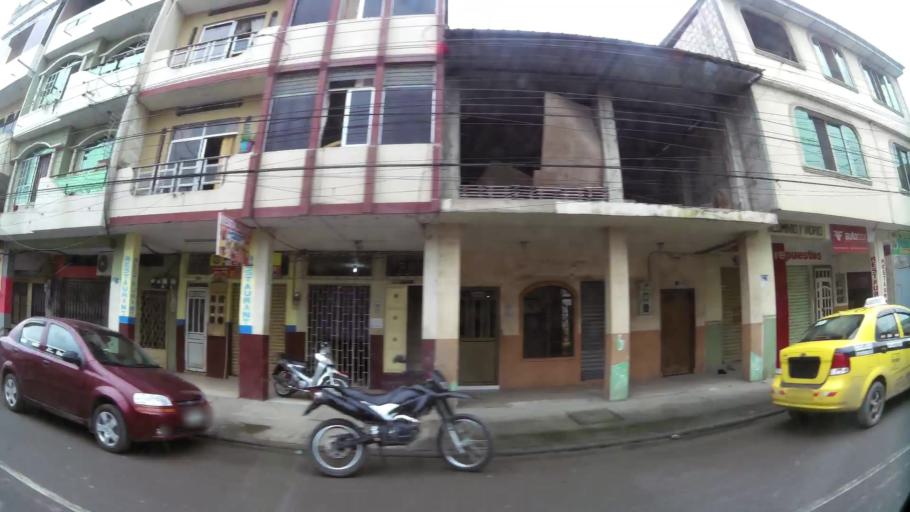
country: EC
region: El Oro
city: Pasaje
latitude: -3.3297
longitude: -79.8068
